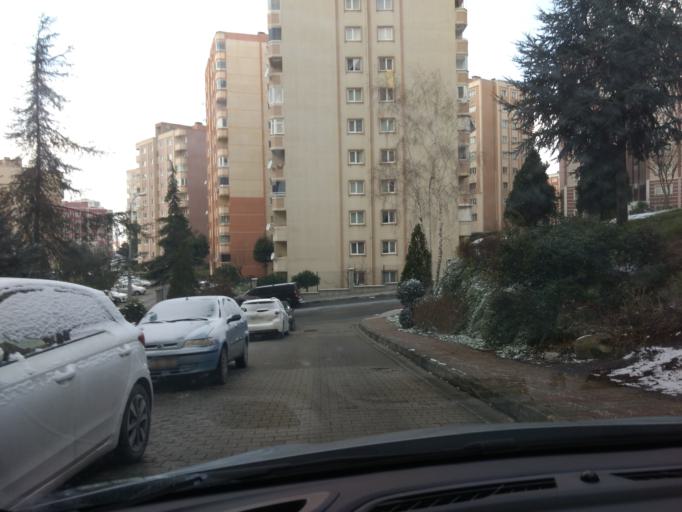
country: TR
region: Istanbul
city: Basaksehir
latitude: 41.1066
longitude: 28.8110
